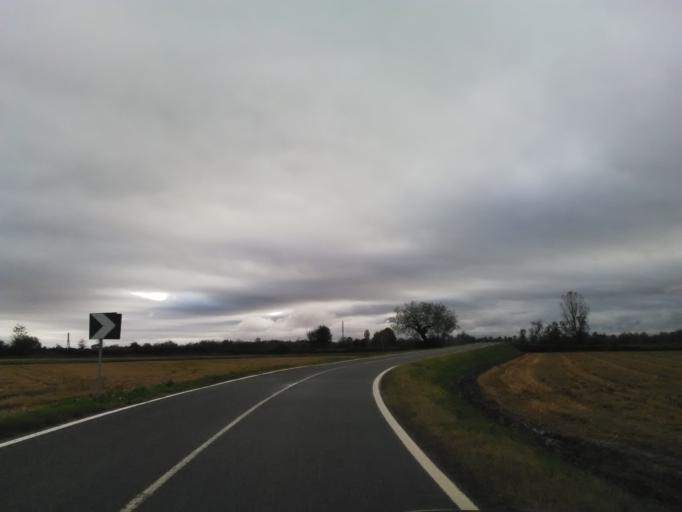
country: IT
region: Piedmont
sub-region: Provincia di Vercelli
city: Casanova Elvo
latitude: 45.4060
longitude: 8.2588
